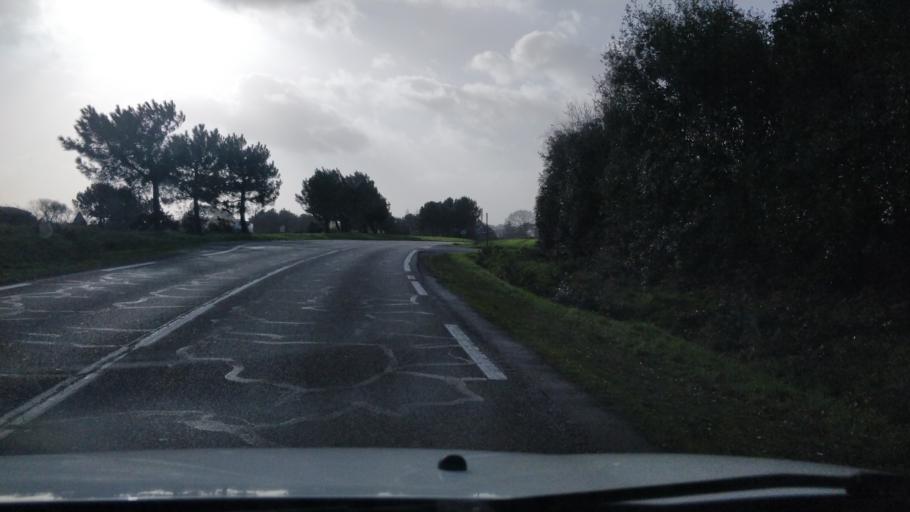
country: FR
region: Pays de la Loire
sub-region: Departement de la Loire-Atlantique
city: Guerande
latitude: 47.3435
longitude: -2.4281
